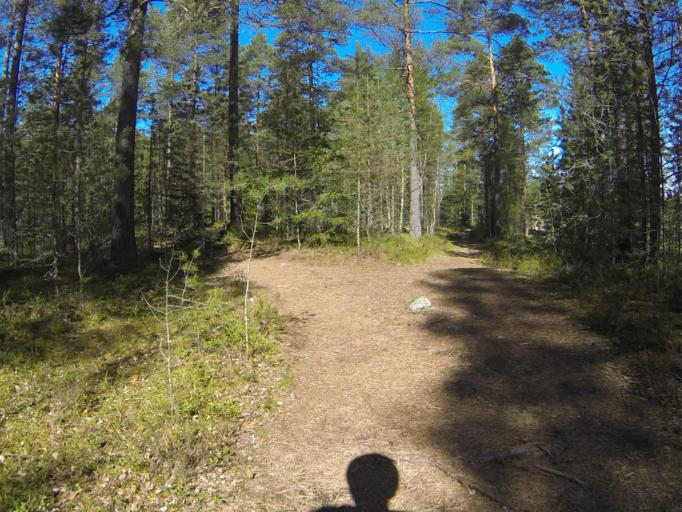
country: FI
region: Varsinais-Suomi
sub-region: Salo
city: Salo
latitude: 60.3997
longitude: 23.1934
